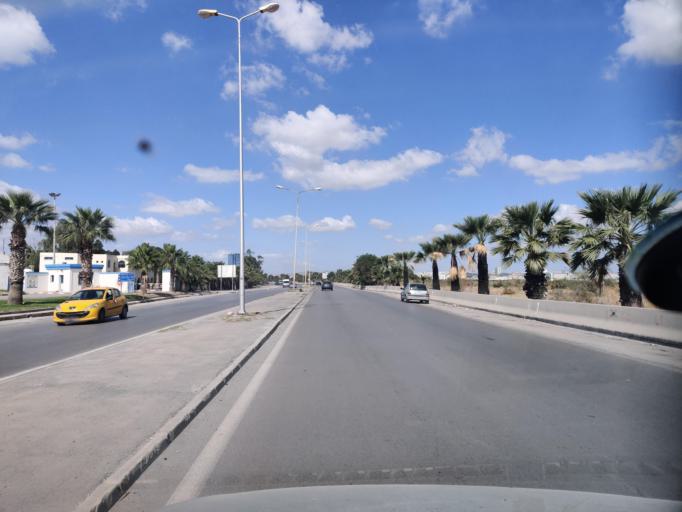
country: TN
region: Bin 'Arus
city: Ben Arous
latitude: 36.7792
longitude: 10.2044
